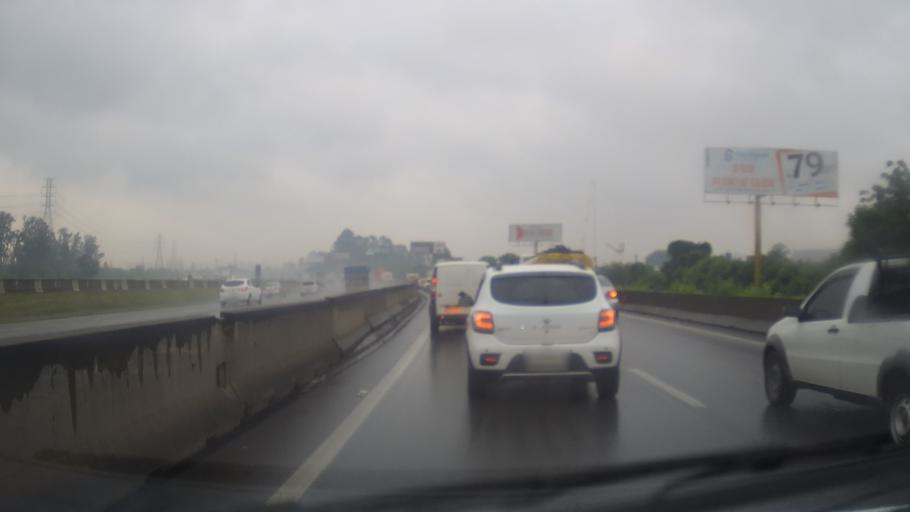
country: BR
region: Sao Paulo
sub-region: Guarulhos
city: Guarulhos
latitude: -23.4737
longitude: -46.4789
